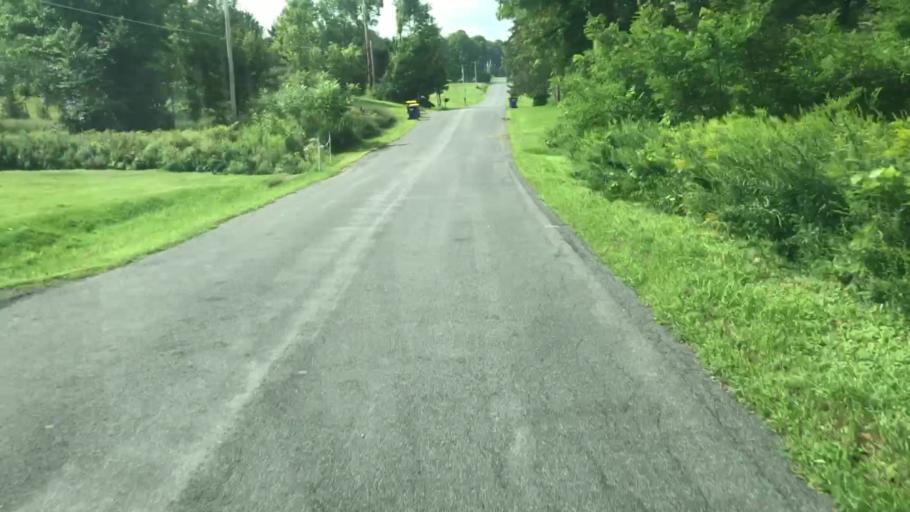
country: US
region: New York
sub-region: Onondaga County
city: Camillus
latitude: 43.0686
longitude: -76.3478
